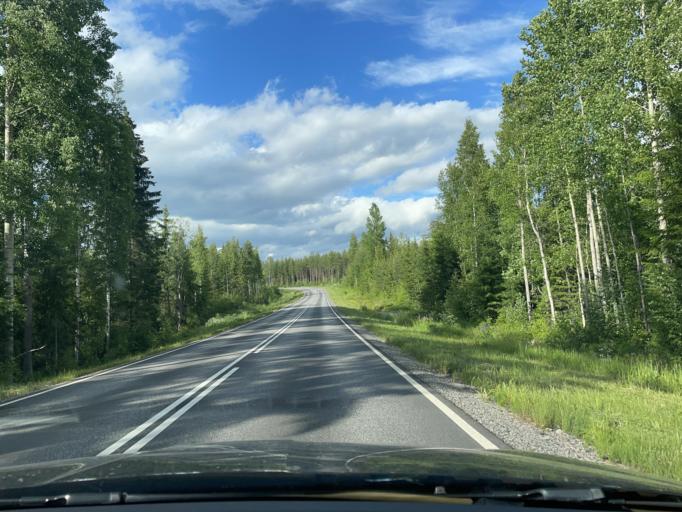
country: FI
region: Central Finland
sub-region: Jyvaeskylae
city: Petaejaevesi
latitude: 62.0953
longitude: 25.1611
